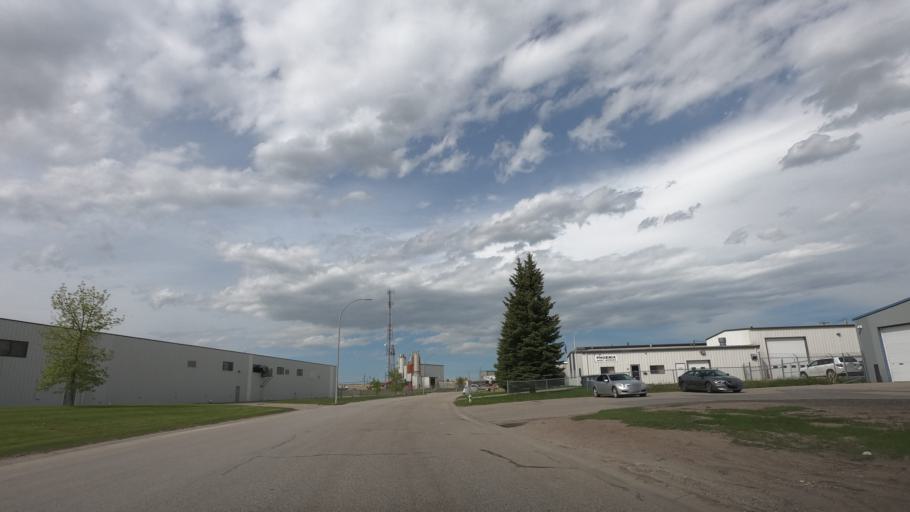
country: CA
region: Alberta
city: Airdrie
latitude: 51.2896
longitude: -113.9876
